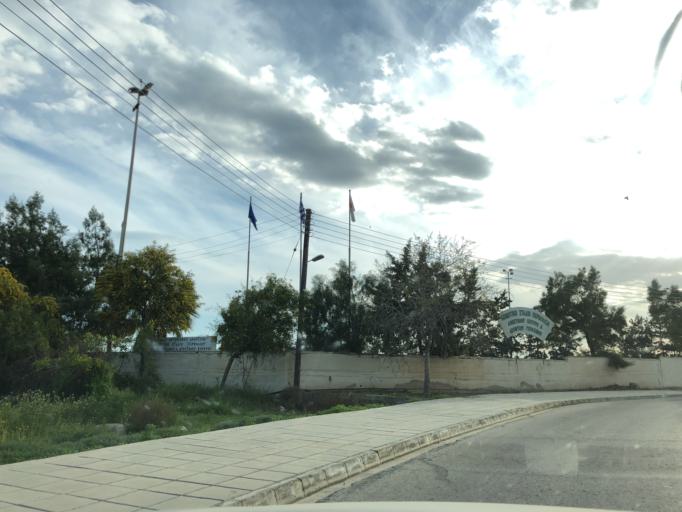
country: CY
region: Larnaka
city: Perivolia
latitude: 34.8267
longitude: 33.5770
